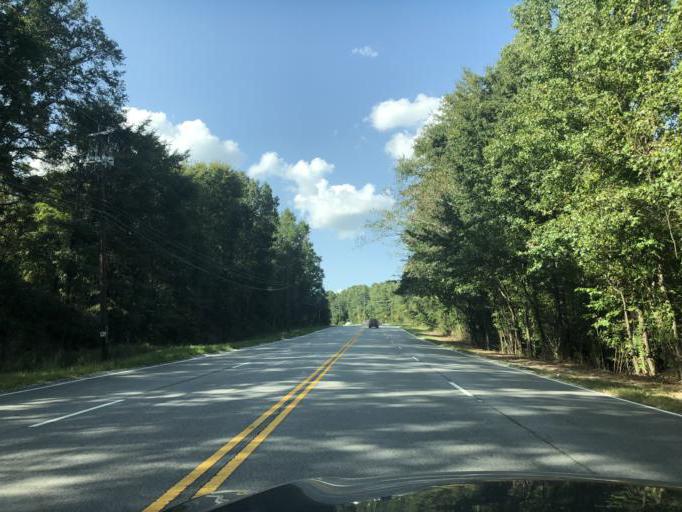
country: US
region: Georgia
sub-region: Muscogee County
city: Columbus
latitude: 32.5066
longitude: -84.8915
